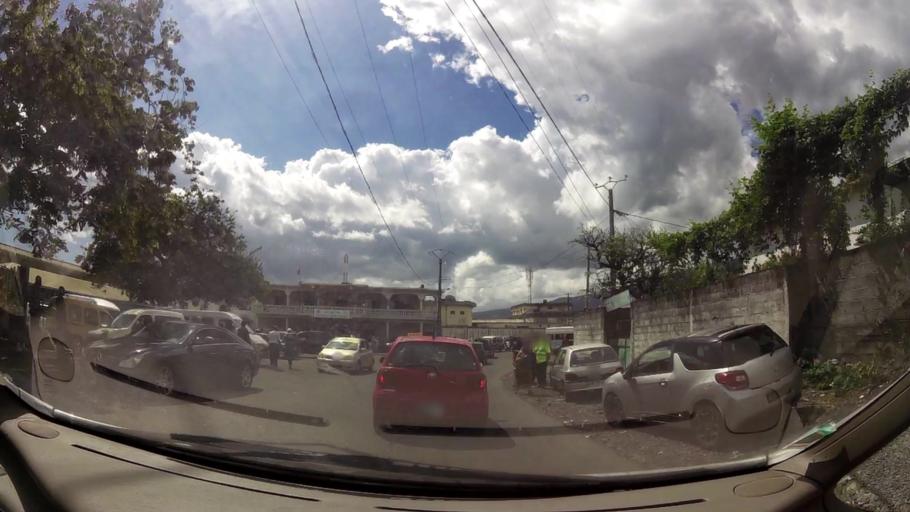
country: KM
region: Grande Comore
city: Moroni
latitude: -11.7064
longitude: 43.2482
